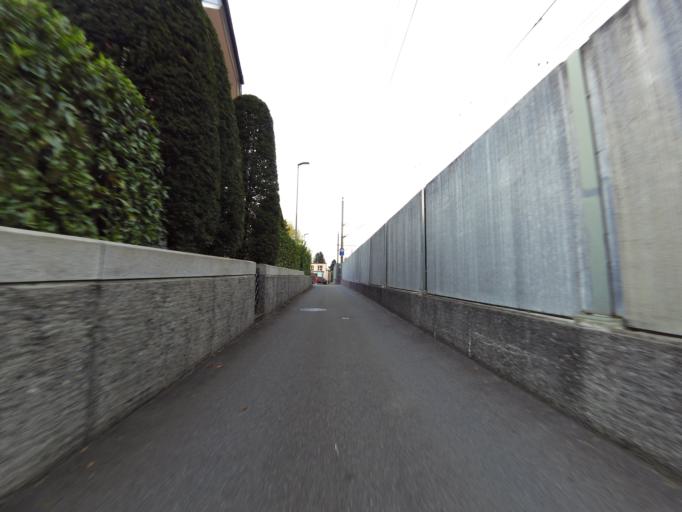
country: CH
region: Uri
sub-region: Uri
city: Flueelen
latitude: 46.9089
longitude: 8.6236
